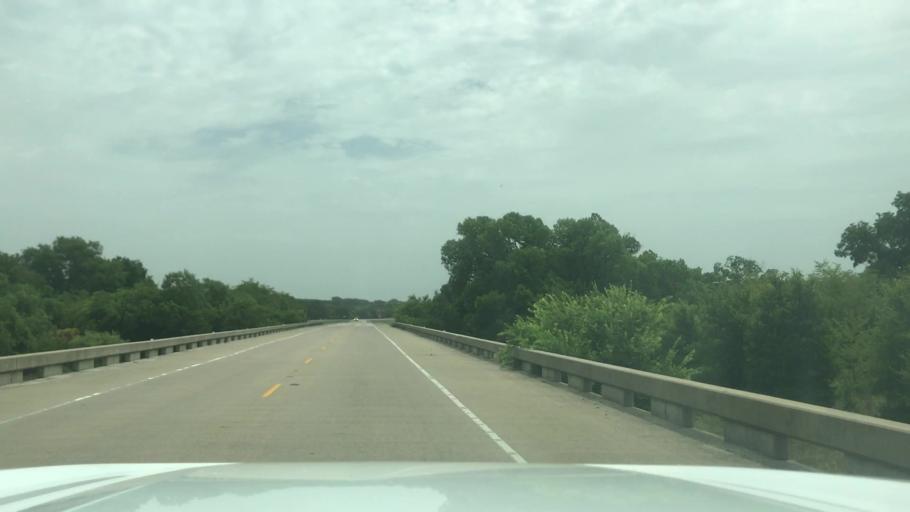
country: US
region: Texas
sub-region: Hamilton County
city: Hico
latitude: 32.0393
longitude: -98.1089
